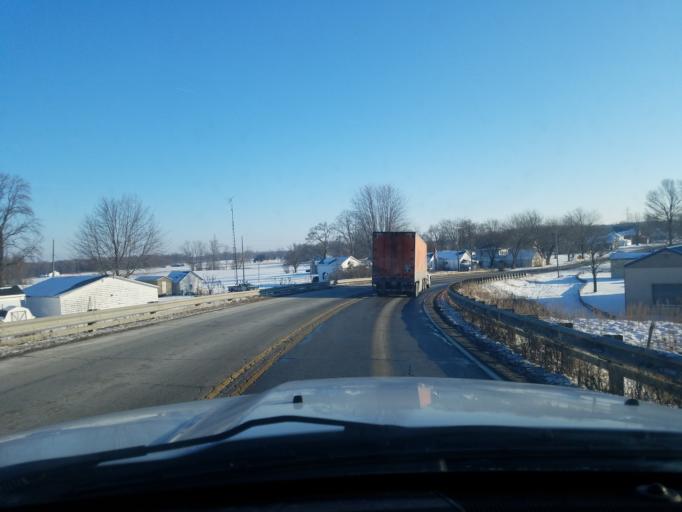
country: US
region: Indiana
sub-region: Noble County
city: Rome City
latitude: 41.4540
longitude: -85.4031
